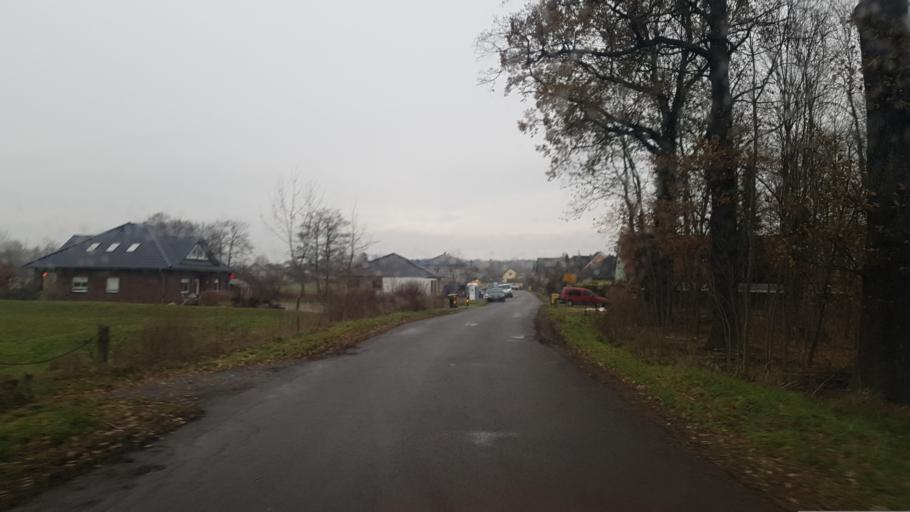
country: DE
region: Brandenburg
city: Drebkau
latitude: 51.6877
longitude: 14.2819
